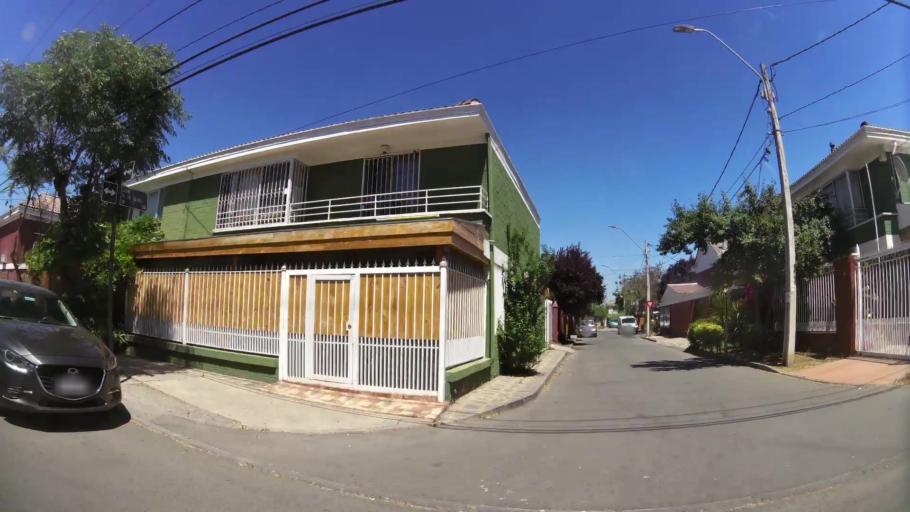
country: CL
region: Santiago Metropolitan
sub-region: Provincia de Maipo
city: San Bernardo
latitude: -33.6222
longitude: -70.7109
